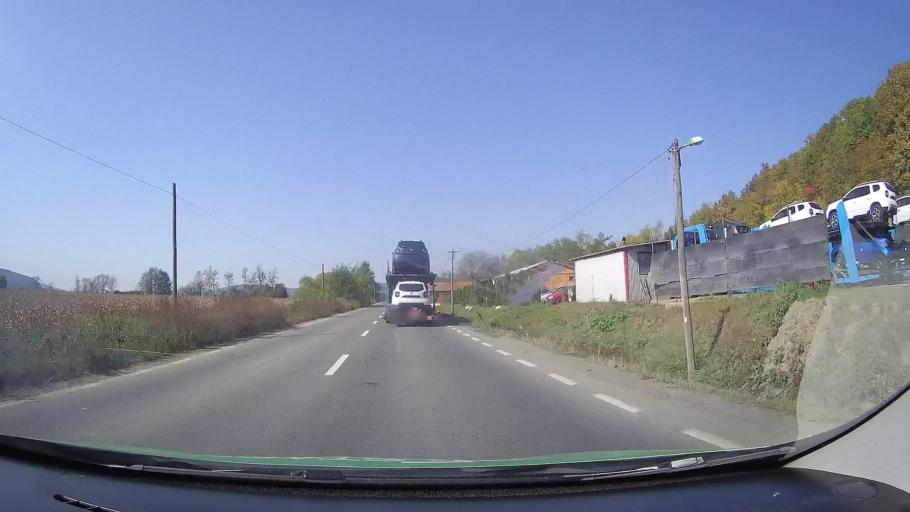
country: RO
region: Arad
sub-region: Comuna Barzava
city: Barzava
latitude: 46.1000
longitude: 22.0129
